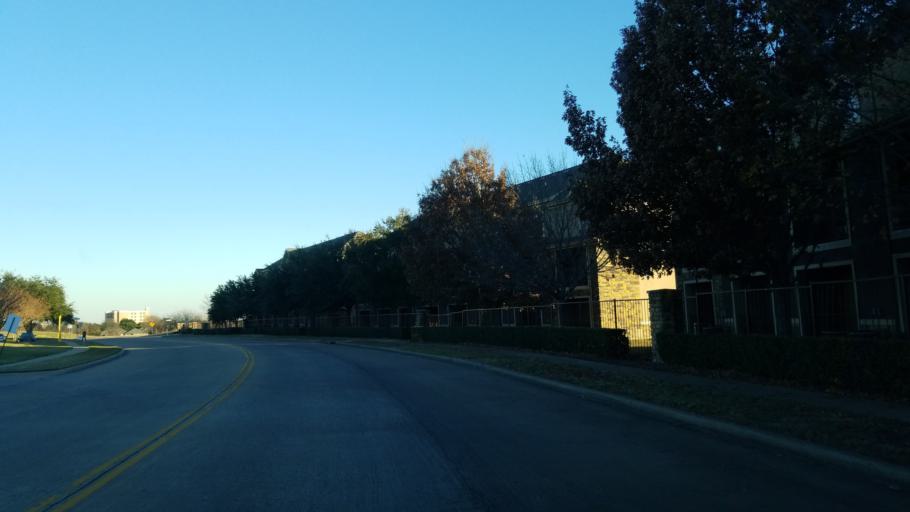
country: US
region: Texas
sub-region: Tarrant County
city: Arlington
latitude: 32.7333
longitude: -97.0585
